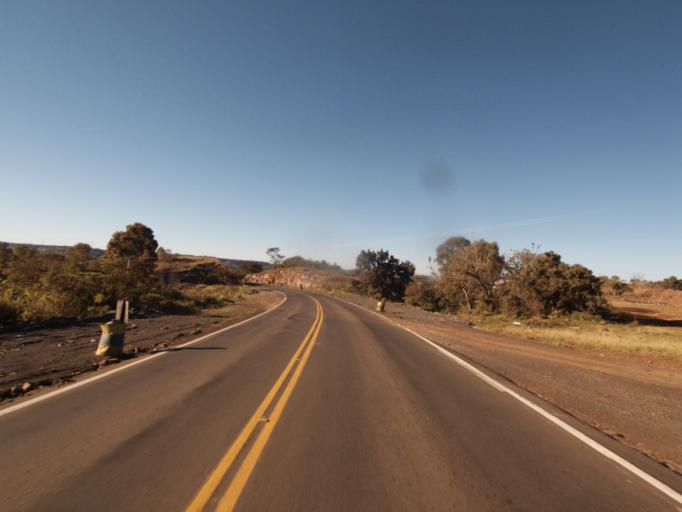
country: AR
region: Misiones
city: Bernardo de Irigoyen
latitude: -26.4963
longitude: -53.5025
